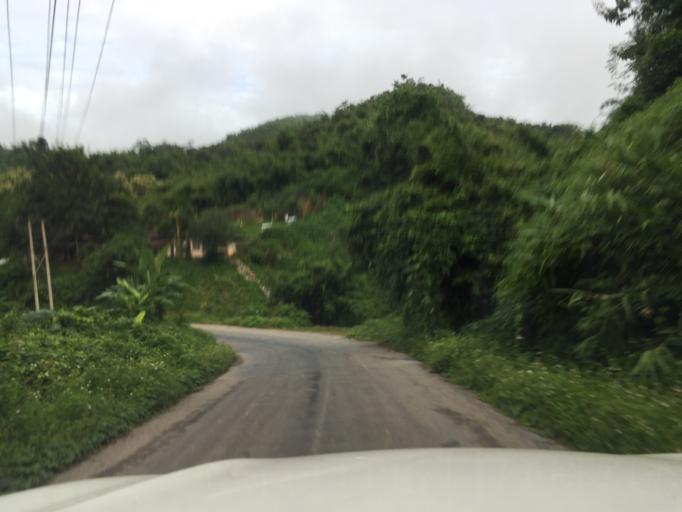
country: LA
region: Phongsali
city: Khoa
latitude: 21.1040
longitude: 102.2744
